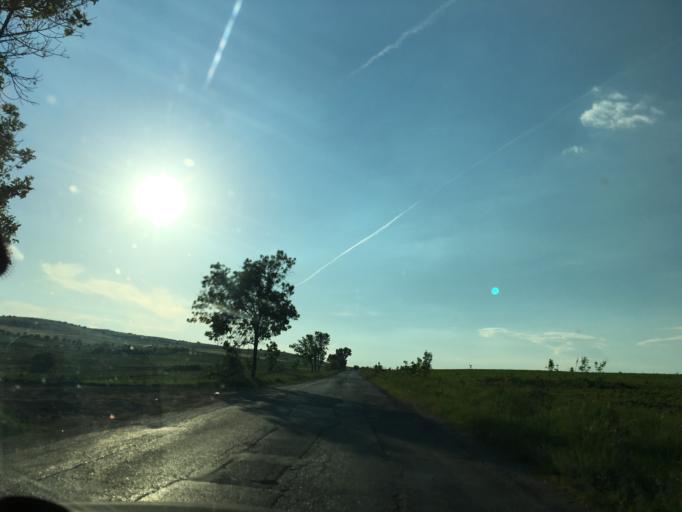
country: BG
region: Sofiya
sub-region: Obshtina Bozhurishte
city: Bozhurishte
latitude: 42.7249
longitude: 23.1226
